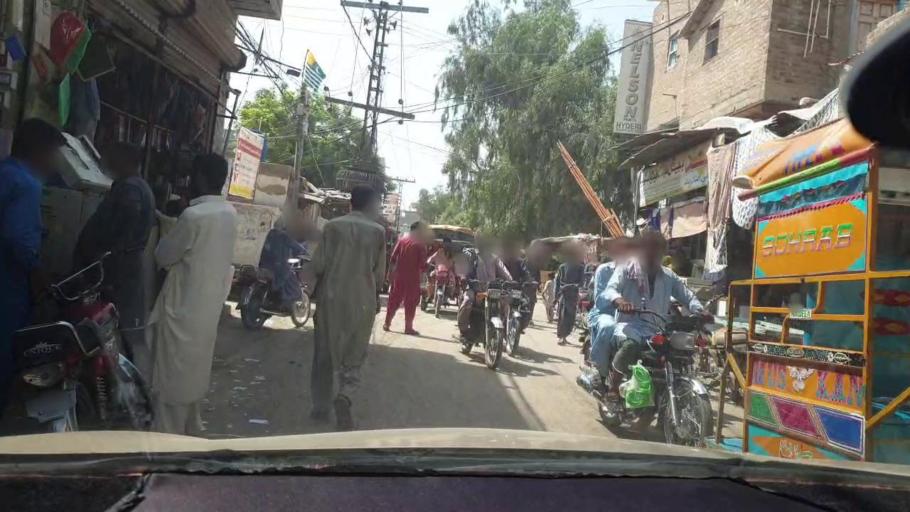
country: PK
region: Sindh
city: Kambar
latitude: 27.5900
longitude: 68.0020
